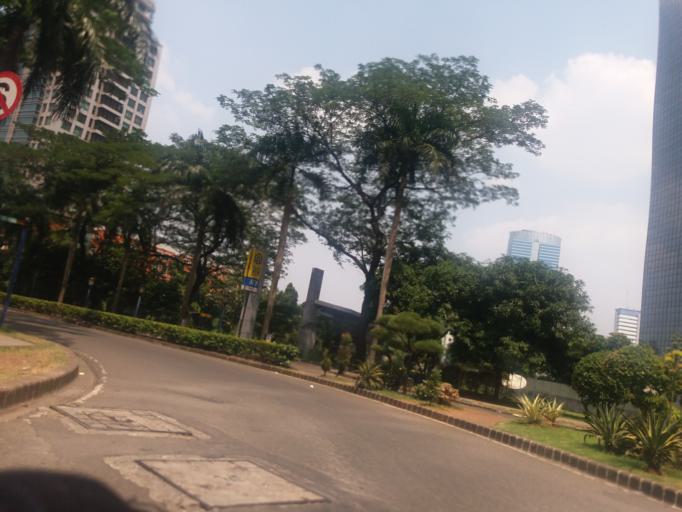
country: ID
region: Jakarta Raya
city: Jakarta
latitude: -6.2298
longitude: 106.8272
